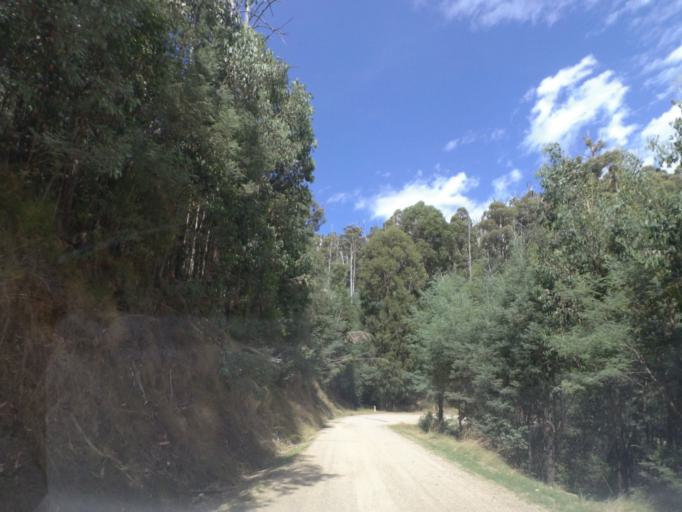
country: AU
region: Victoria
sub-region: Murrindindi
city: Alexandra
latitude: -37.4637
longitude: 145.7876
